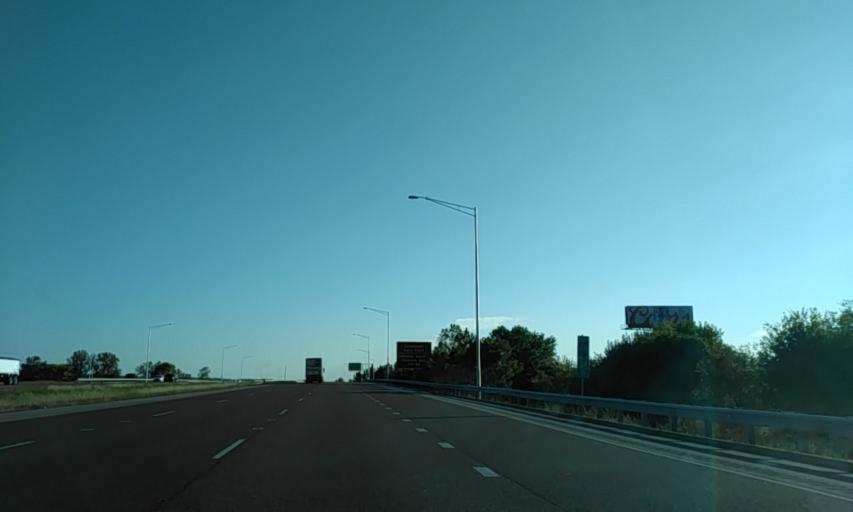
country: US
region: Illinois
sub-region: Saint Clair County
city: Caseyville
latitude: 38.6622
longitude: -90.0305
